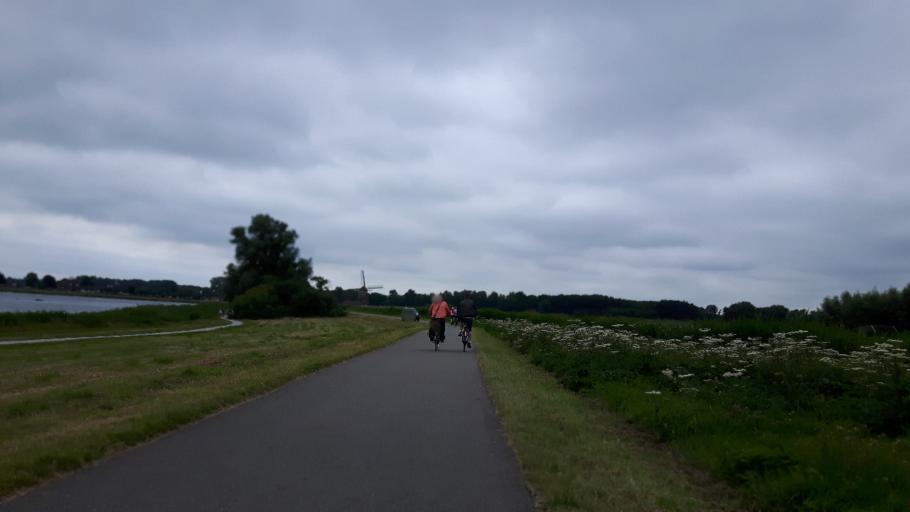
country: NL
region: South Holland
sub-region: Gemeente Lansingerland
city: Bleiswijk
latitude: 52.0056
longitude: 4.5600
